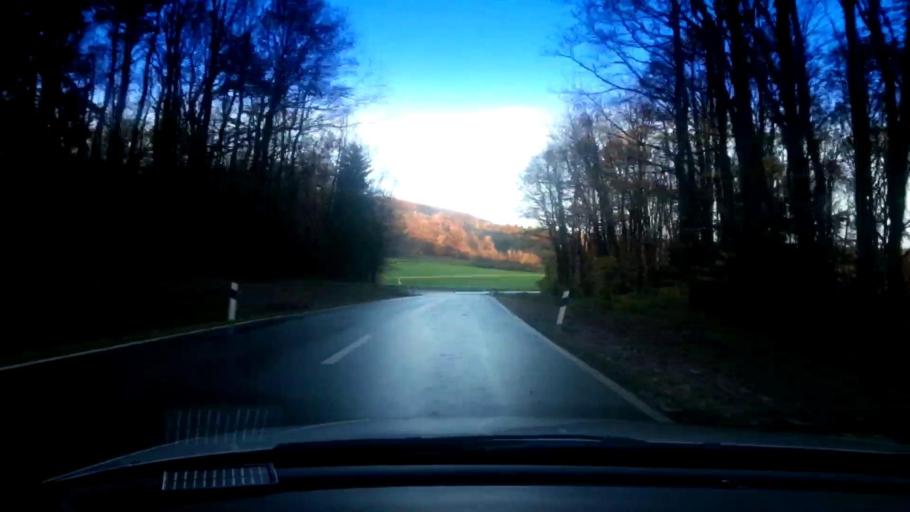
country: DE
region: Bavaria
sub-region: Upper Franconia
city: Buttenheim
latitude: 49.8249
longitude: 11.0478
